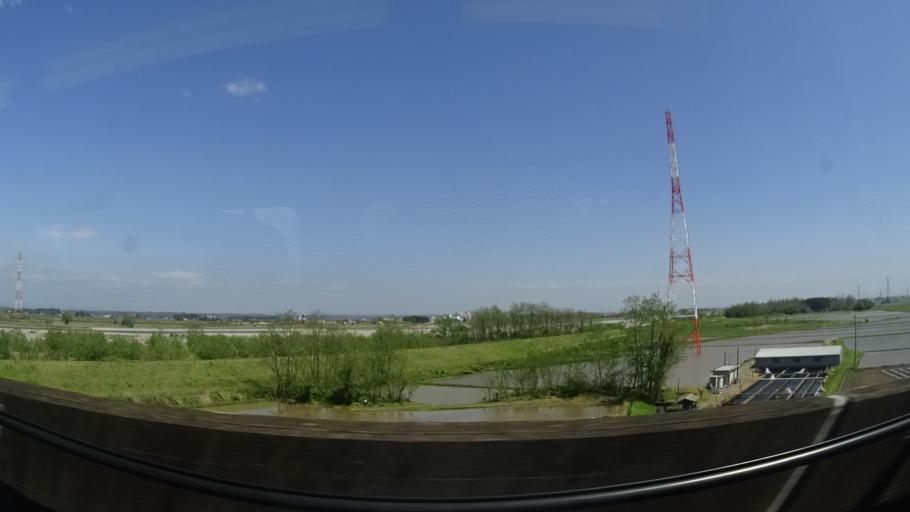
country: JP
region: Tochigi
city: Ujiie
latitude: 36.7036
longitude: 139.9202
